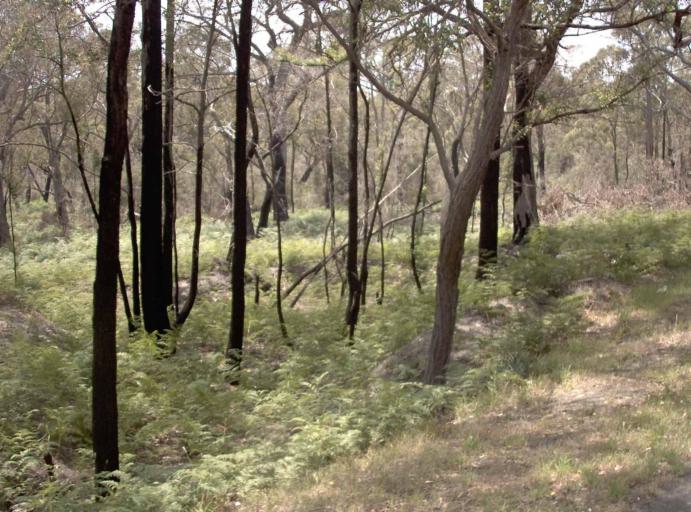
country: AU
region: Victoria
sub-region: Latrobe
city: Traralgon
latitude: -38.2655
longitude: 146.6903
